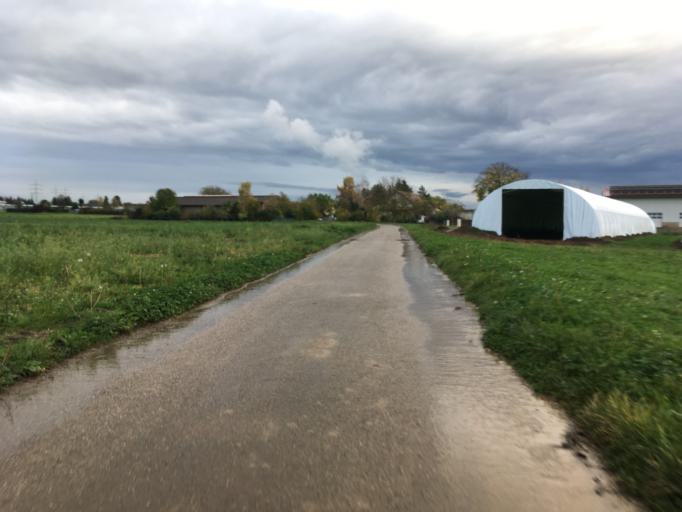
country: DE
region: Baden-Wuerttemberg
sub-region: Regierungsbezirk Stuttgart
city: Nordheim
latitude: 49.1067
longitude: 9.1626
